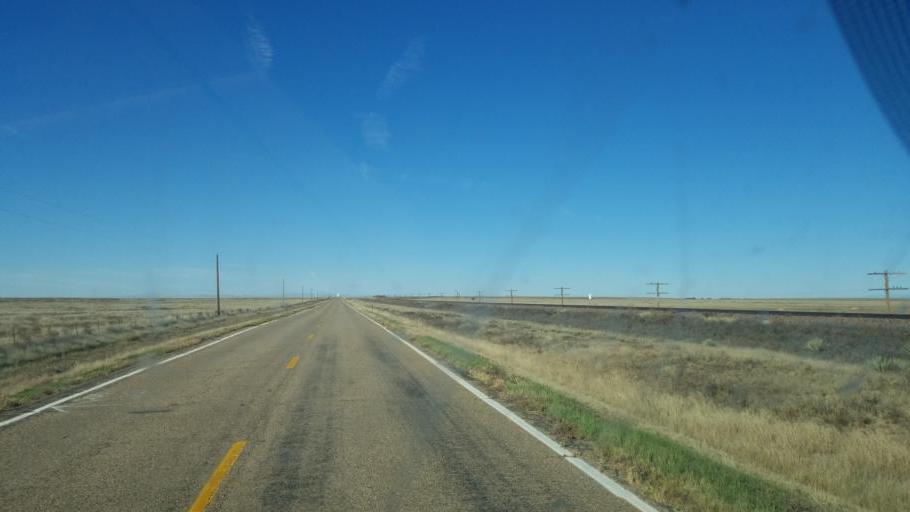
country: US
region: Colorado
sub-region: Crowley County
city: Ordway
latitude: 38.2455
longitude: -103.6049
